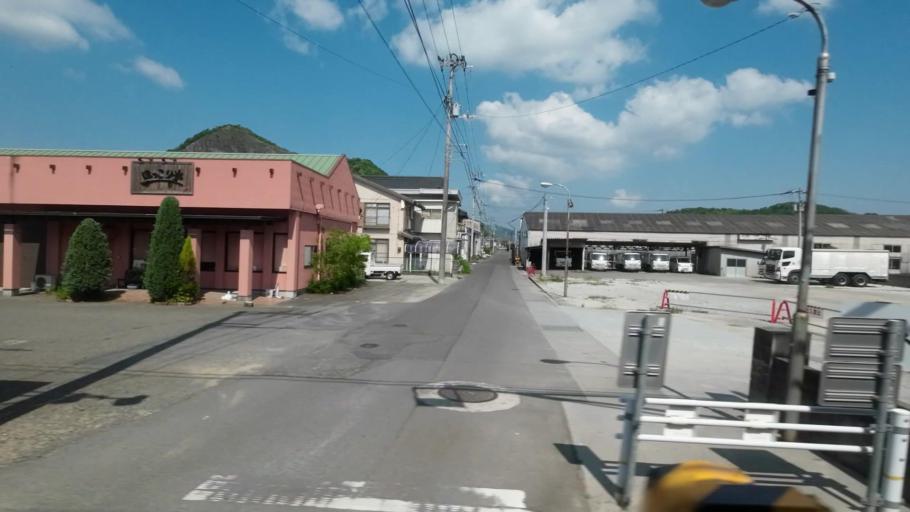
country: JP
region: Kagawa
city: Kan'onjicho
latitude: 34.1859
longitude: 133.7126
